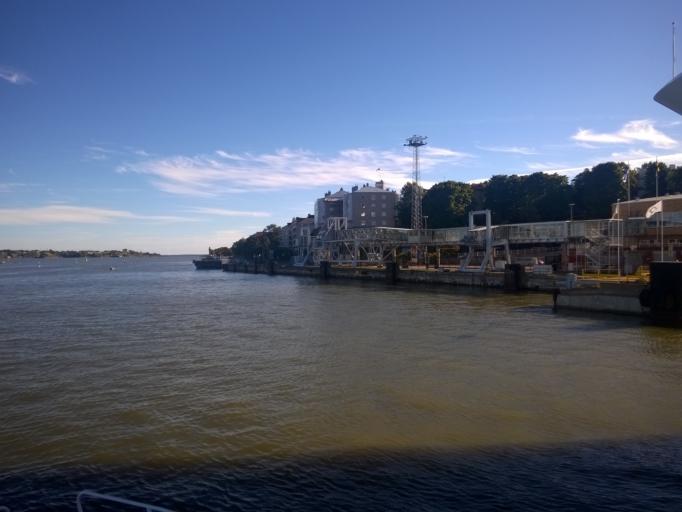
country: FI
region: Uusimaa
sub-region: Helsinki
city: Helsinki
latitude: 60.1615
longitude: 24.9603
